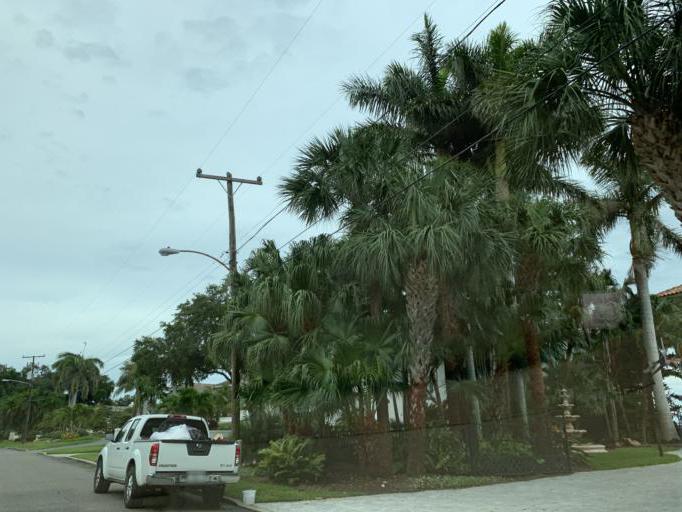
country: US
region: Florida
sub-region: Pinellas County
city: Saint Petersburg
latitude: 27.7911
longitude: -82.6111
